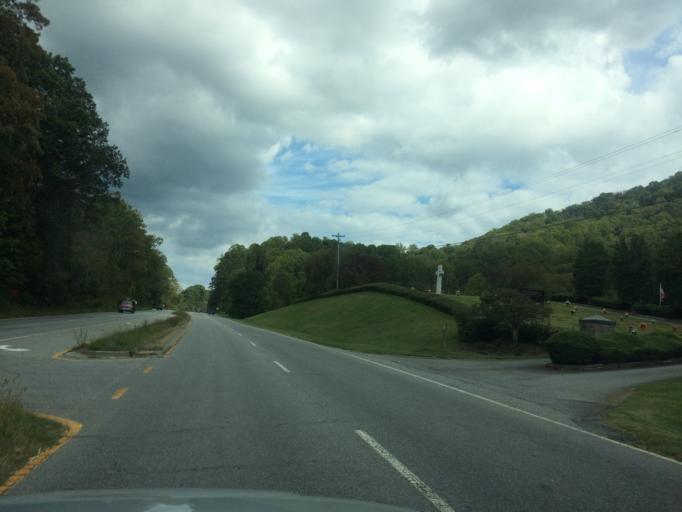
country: US
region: North Carolina
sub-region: Haywood County
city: Clyde
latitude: 35.5297
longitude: -82.8936
